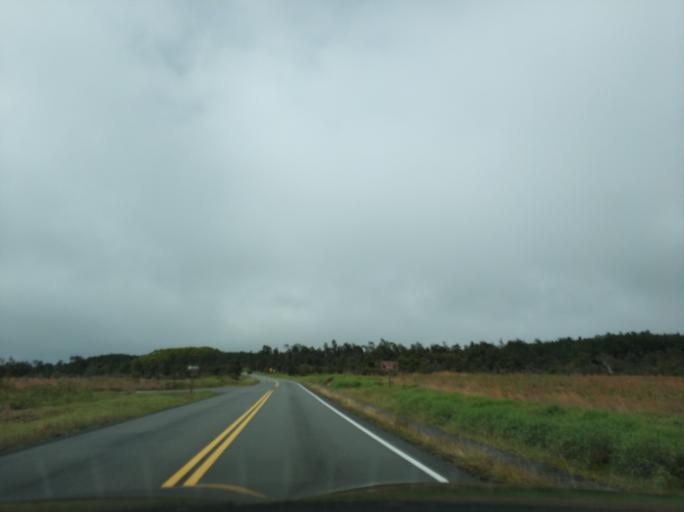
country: US
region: Hawaii
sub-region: Hawaii County
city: Volcano
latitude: 19.4319
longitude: -155.2680
